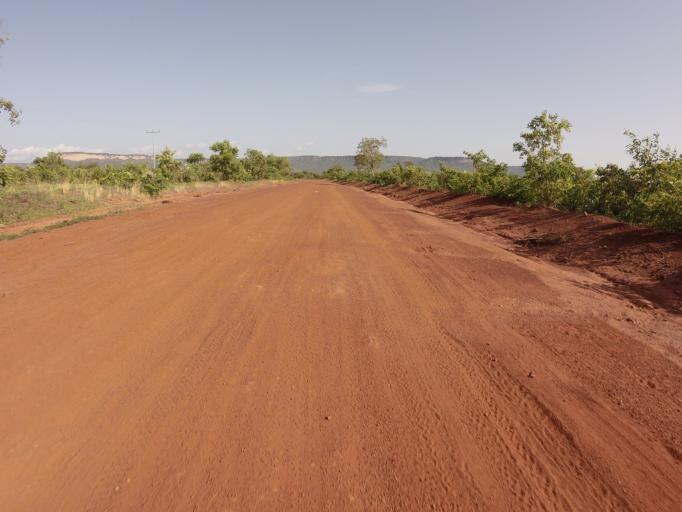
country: GH
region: Upper East
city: Bawku
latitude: 10.6859
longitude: -0.2156
